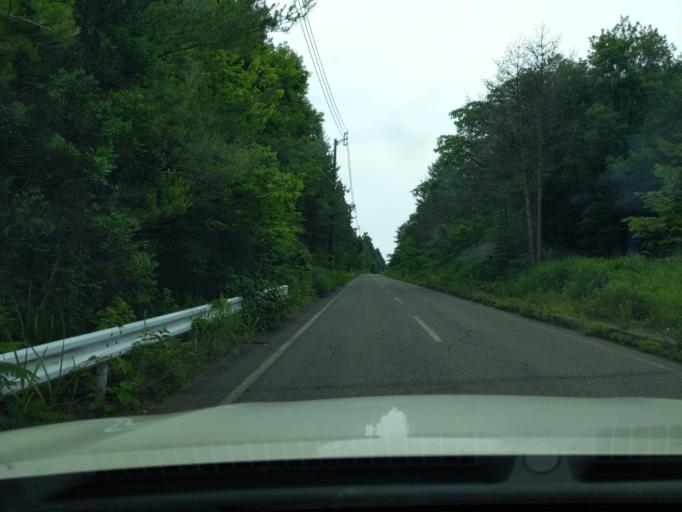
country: JP
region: Niigata
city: Kashiwazaki
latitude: 37.3336
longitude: 138.5844
